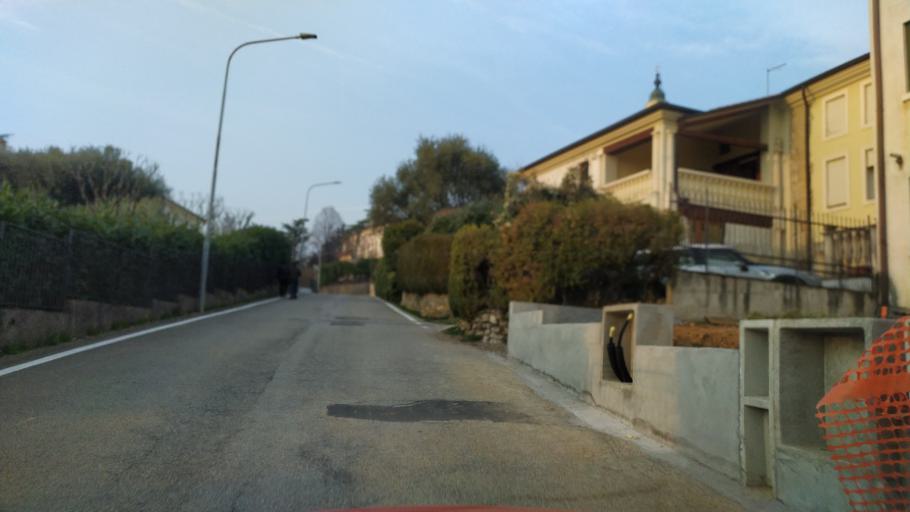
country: IT
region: Veneto
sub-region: Provincia di Vicenza
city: Sarcedo
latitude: 45.7061
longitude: 11.5261
